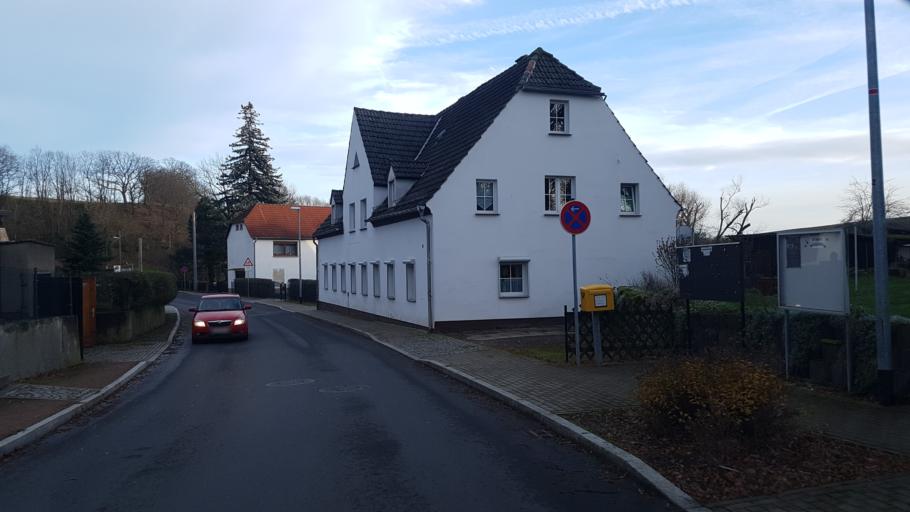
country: DE
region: Saxony
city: Ostrau
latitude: 51.1673
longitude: 13.1617
